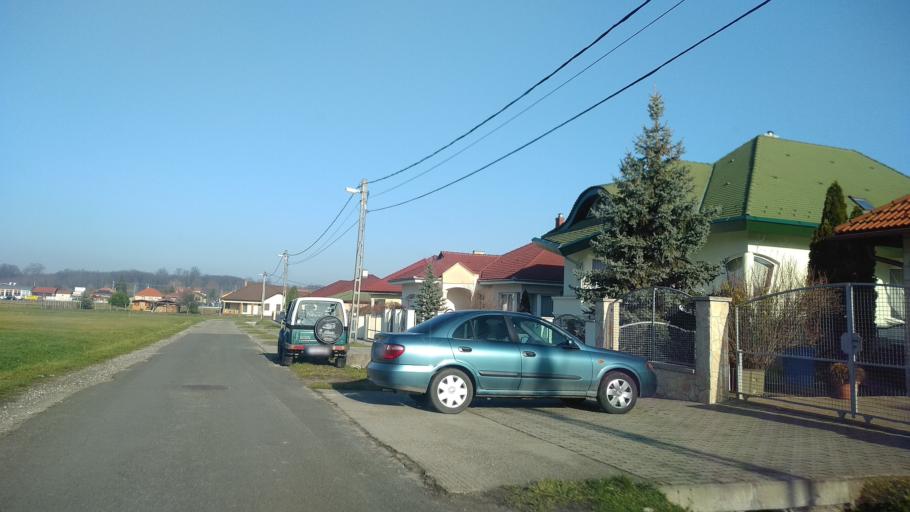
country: HU
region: Somogy
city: Barcs
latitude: 45.9626
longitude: 17.4680
